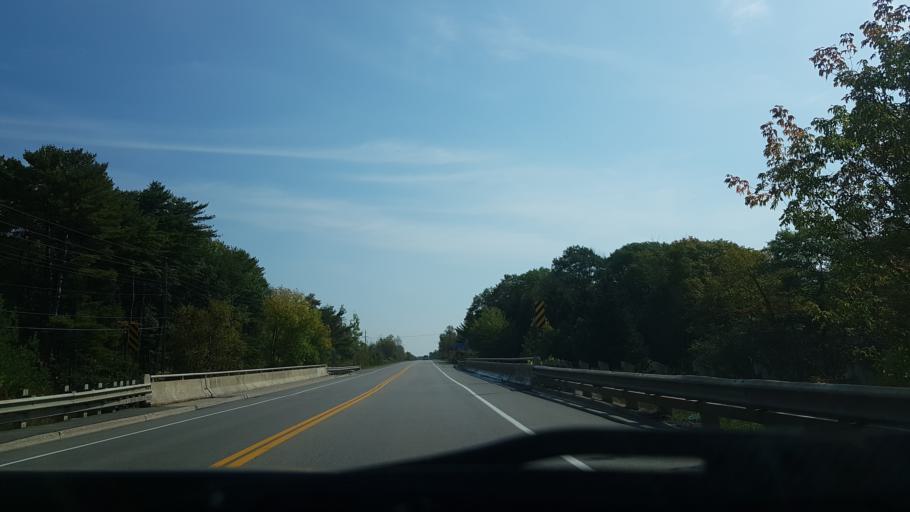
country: CA
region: Ontario
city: Orillia
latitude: 44.7436
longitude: -79.3148
